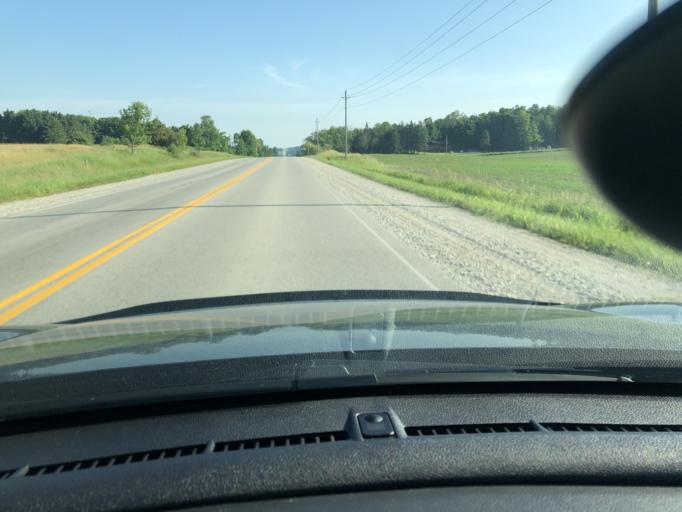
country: CA
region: Ontario
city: Stratford
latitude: 43.4020
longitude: -80.8375
